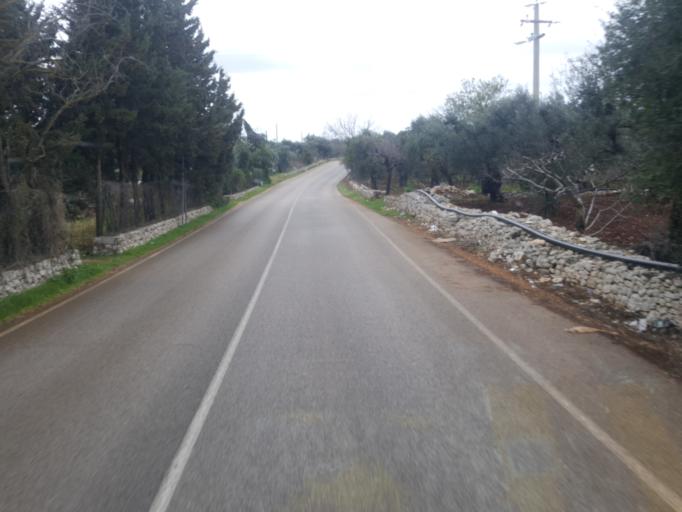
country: IT
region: Apulia
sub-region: Provincia di Bari
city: Conversano
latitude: 40.9501
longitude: 17.0874
